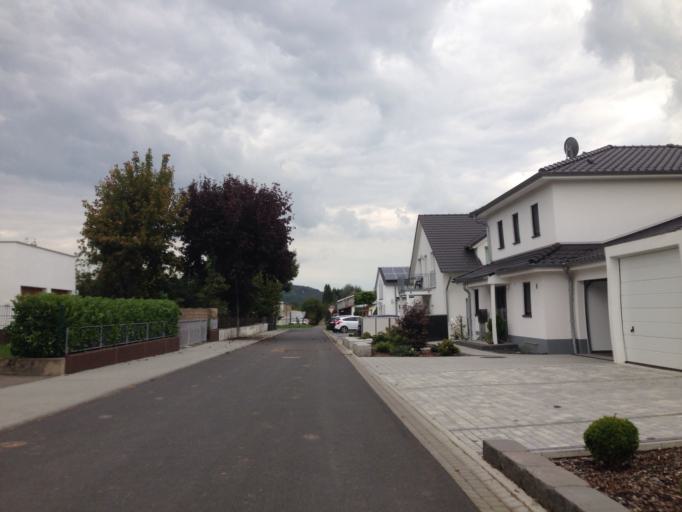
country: DE
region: Hesse
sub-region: Regierungsbezirk Giessen
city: Alten Buseck
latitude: 50.6168
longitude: 8.7516
